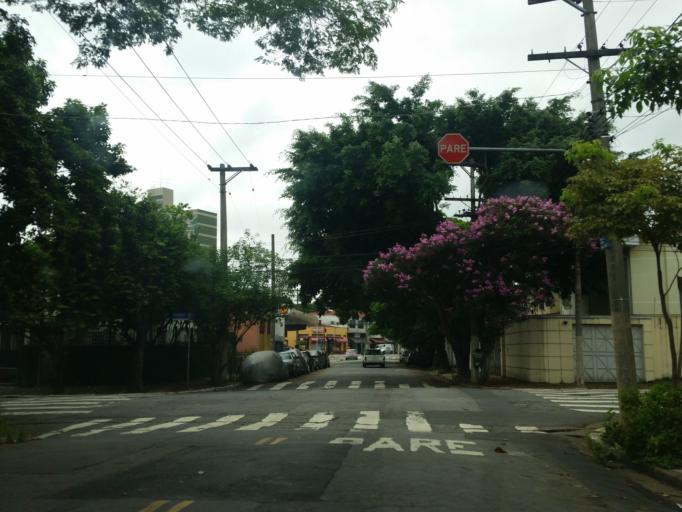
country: BR
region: Sao Paulo
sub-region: Sao Paulo
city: Sao Paulo
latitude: -23.6187
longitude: -46.6514
